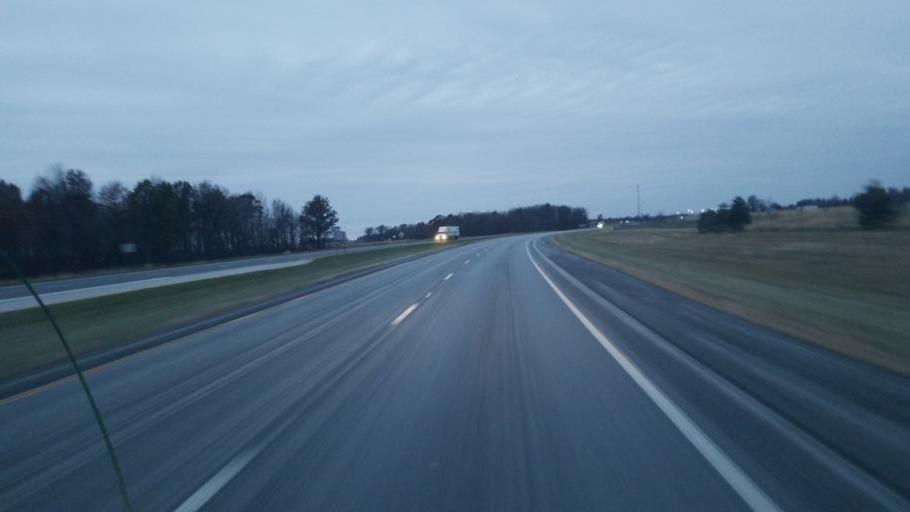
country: US
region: Ohio
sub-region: Hancock County
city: Arlington
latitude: 40.8276
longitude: -83.6020
